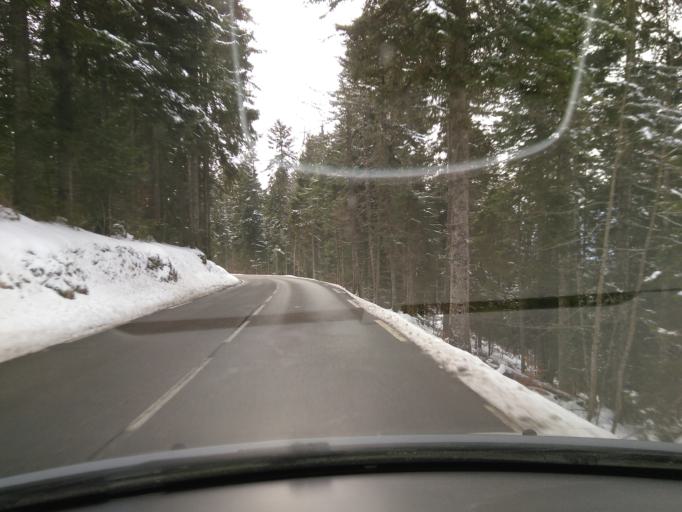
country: FR
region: Rhone-Alpes
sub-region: Departement de l'Isere
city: Le Sappey-en-Chartreuse
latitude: 45.2816
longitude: 5.7665
